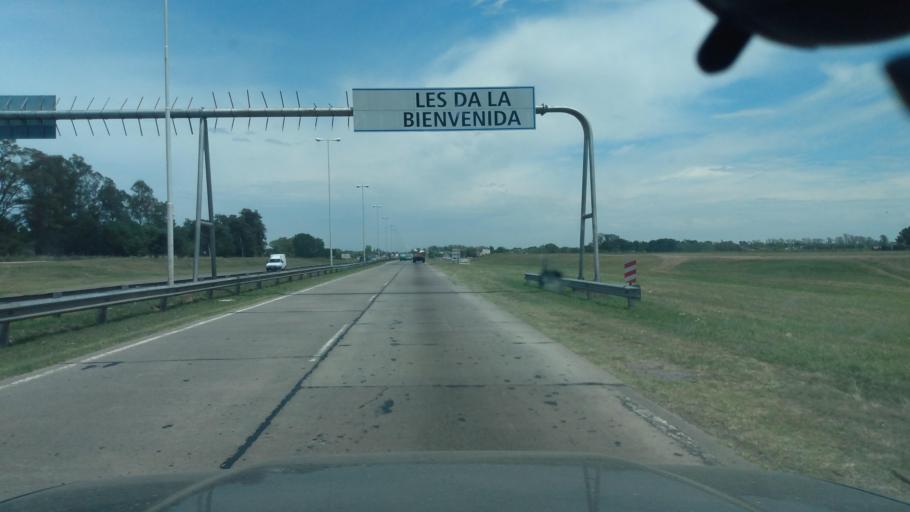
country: AR
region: Buenos Aires
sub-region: Partido de Lujan
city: Lujan
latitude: -34.5662
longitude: -59.0713
